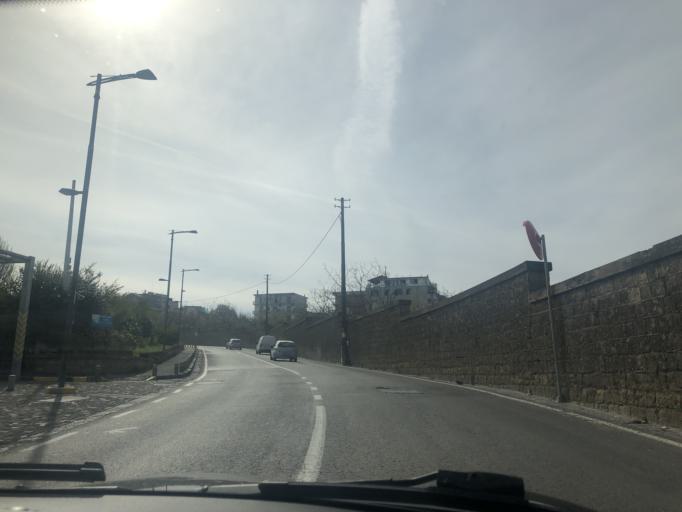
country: IT
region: Campania
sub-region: Provincia di Napoli
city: Torre Caracciolo
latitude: 40.8683
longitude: 14.2055
